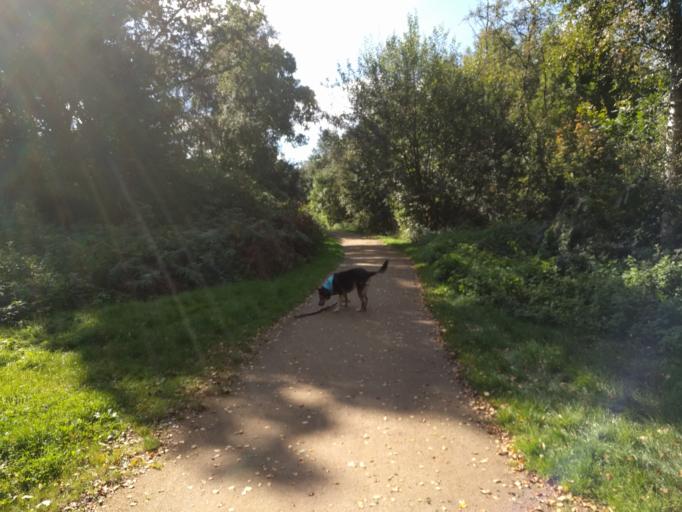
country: GB
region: England
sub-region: Warrington
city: Culcheth
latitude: 53.4236
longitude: -2.5074
